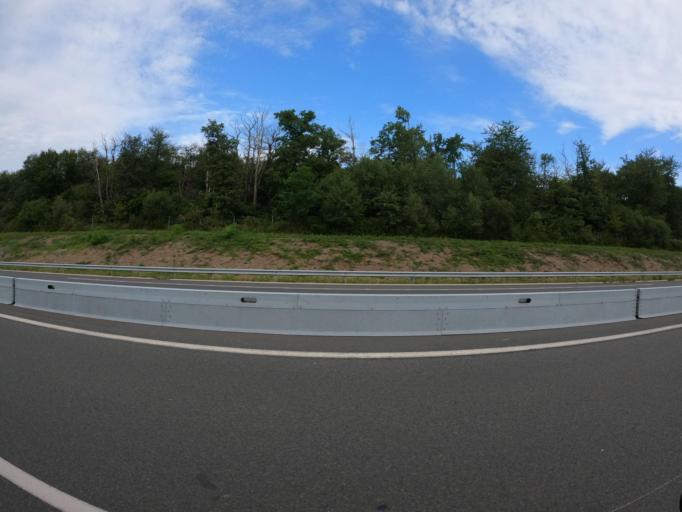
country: FR
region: Centre
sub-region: Departement d'Indre-et-Loire
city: Restigne
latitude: 47.2914
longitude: 0.2849
